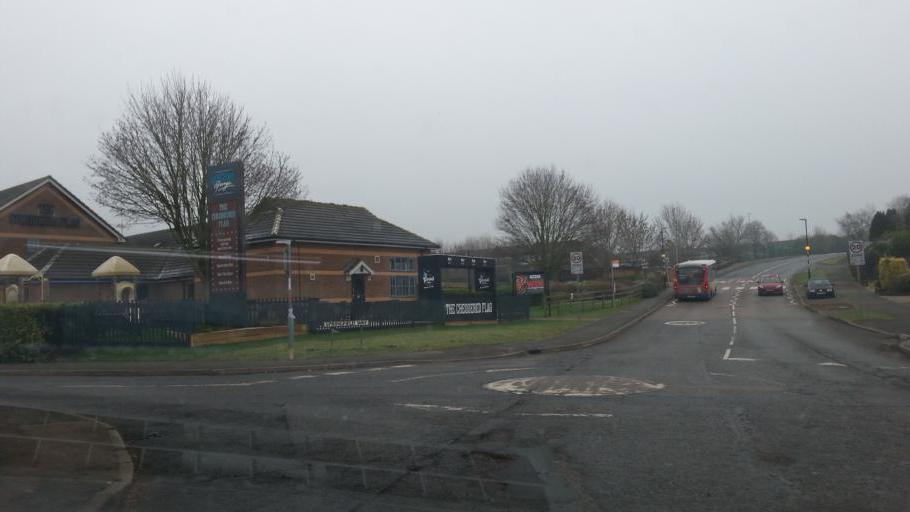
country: GB
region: England
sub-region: Northamptonshire
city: Brackley
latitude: 52.0363
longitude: -1.1541
